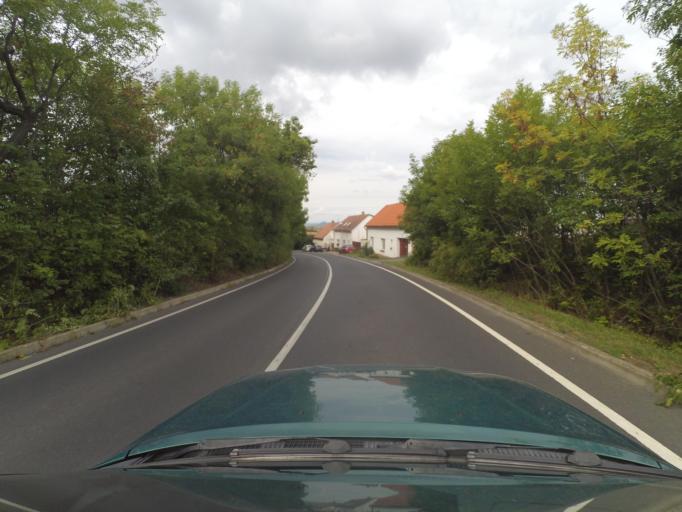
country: CZ
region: Ustecky
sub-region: Okres Louny
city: Louny
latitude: 50.2904
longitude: 13.7830
